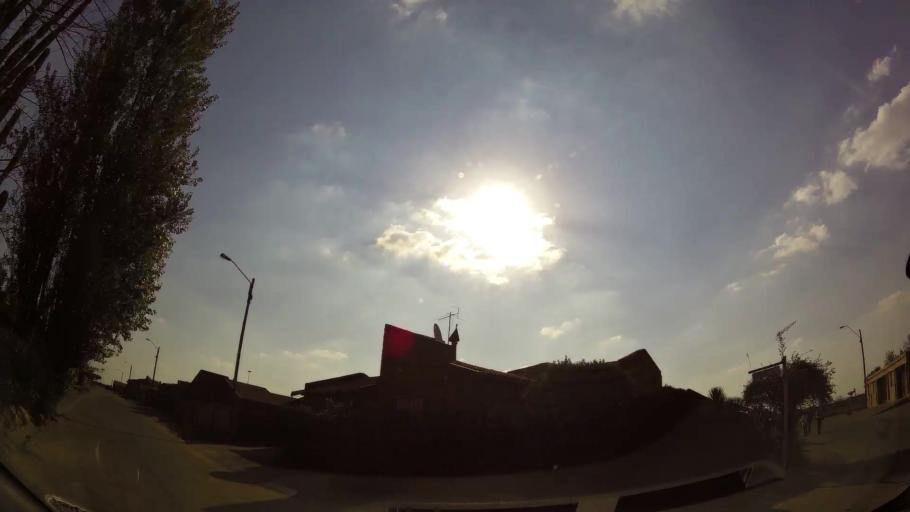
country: ZA
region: Gauteng
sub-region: Ekurhuleni Metropolitan Municipality
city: Benoni
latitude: -26.1516
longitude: 28.4001
